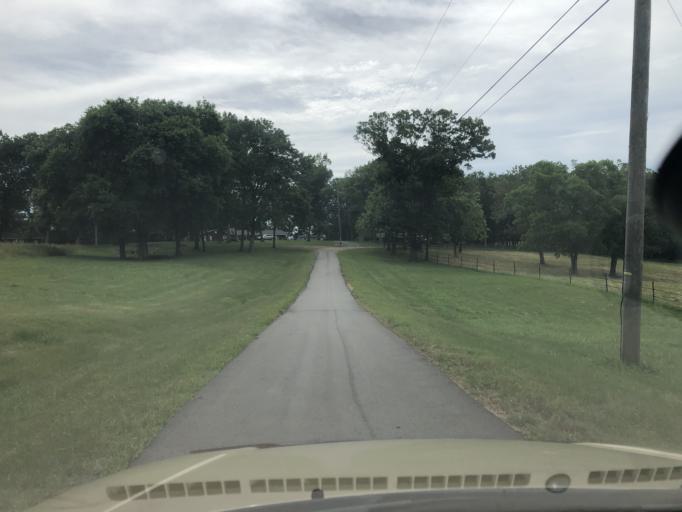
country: US
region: Tennessee
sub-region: Davidson County
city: Lakewood
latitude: 36.2242
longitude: -86.6478
